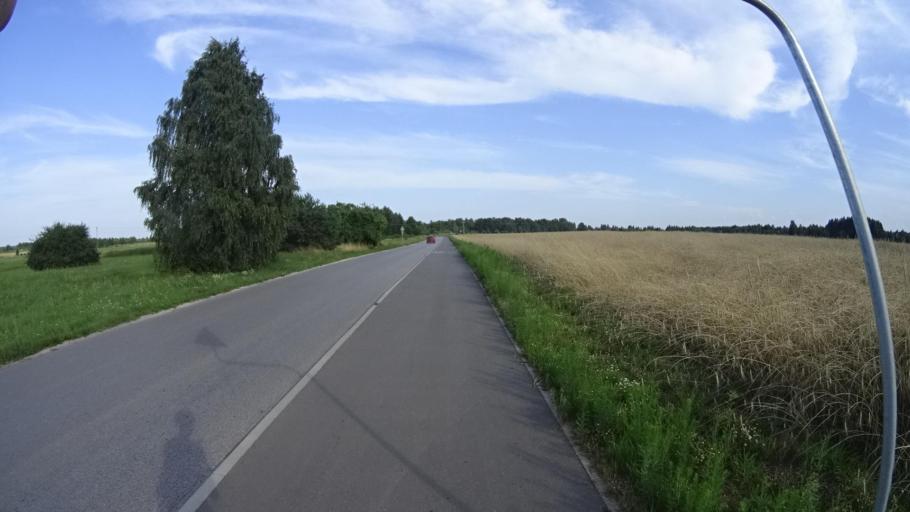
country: PL
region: Masovian Voivodeship
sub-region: Powiat piaseczynski
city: Tarczyn
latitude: 52.0154
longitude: 20.7974
